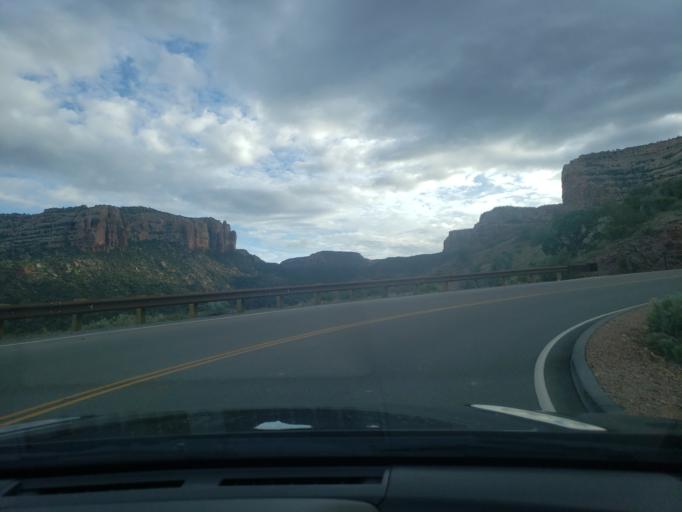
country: US
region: Colorado
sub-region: Mesa County
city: Redlands
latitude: 39.0263
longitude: -108.6378
